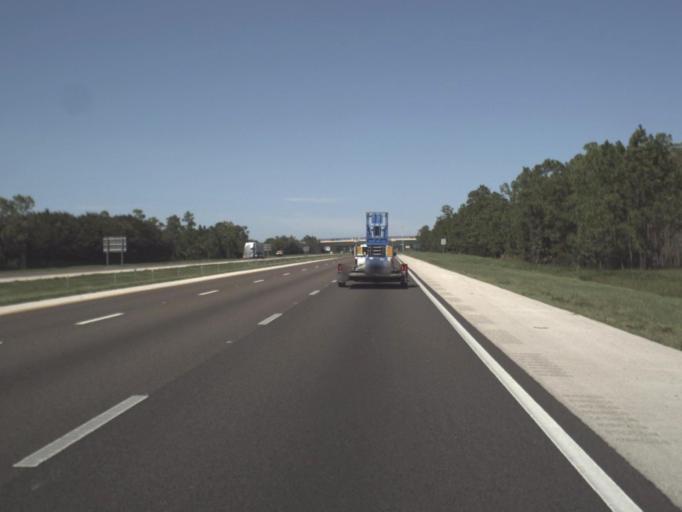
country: US
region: Florida
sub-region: Lee County
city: Estero
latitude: 26.4409
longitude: -81.7808
